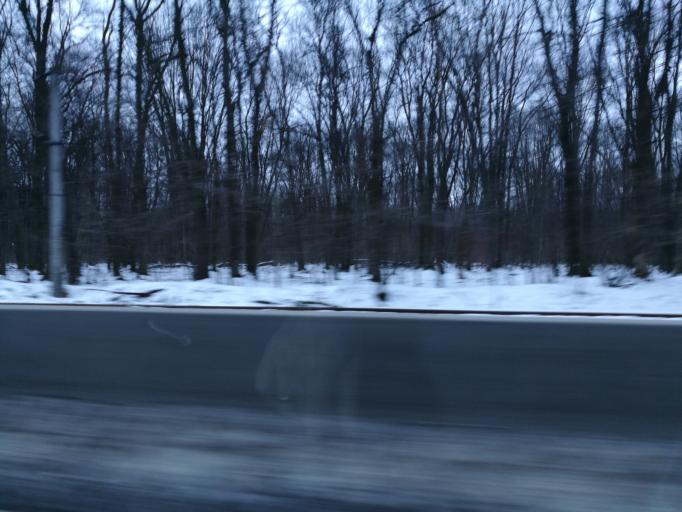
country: RO
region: Ilfov
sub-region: Comuna Tunari
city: Tunari
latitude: 44.5392
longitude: 26.1143
